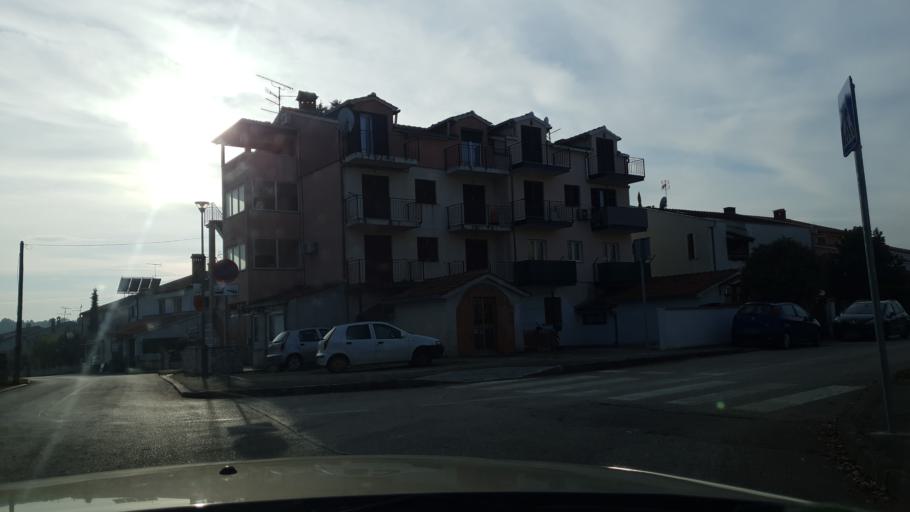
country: HR
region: Istarska
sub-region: Grad Porec
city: Porec
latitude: 45.2335
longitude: 13.6099
